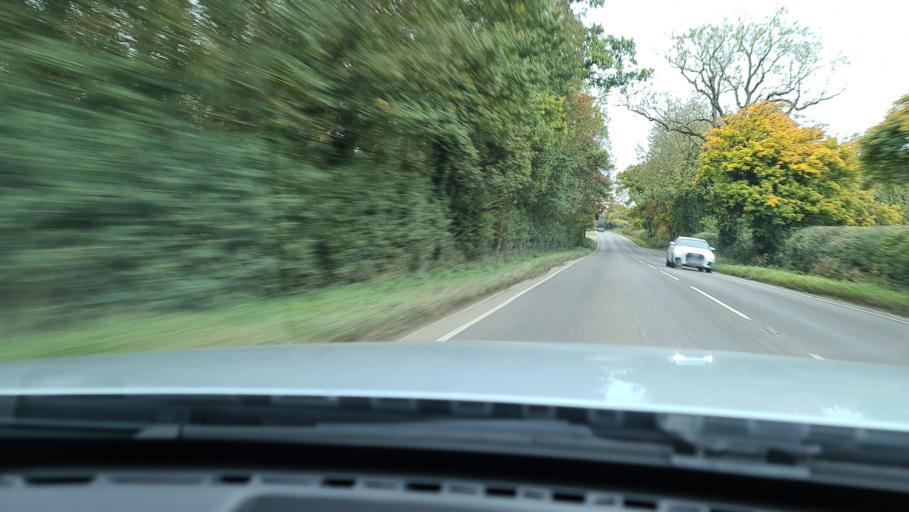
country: GB
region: England
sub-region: Buckinghamshire
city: Waddesdon
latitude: 51.8611
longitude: -0.9891
